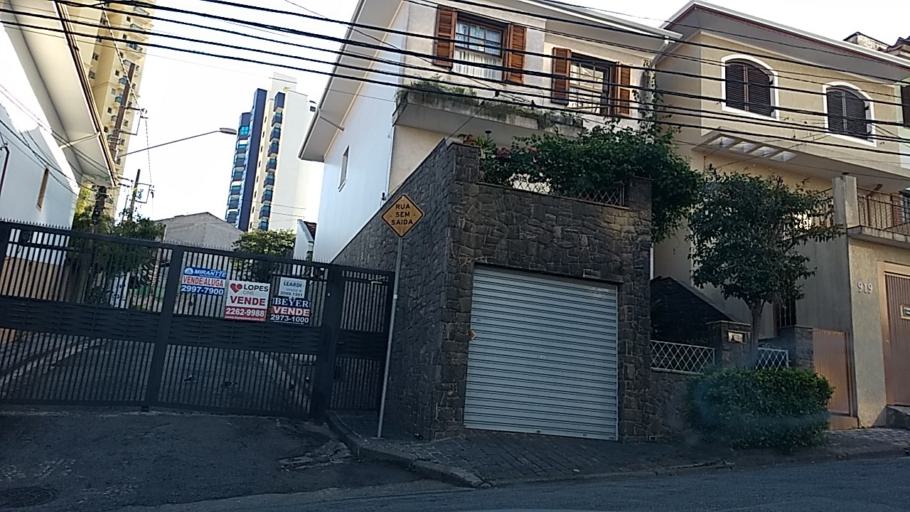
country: BR
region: Sao Paulo
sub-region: Sao Paulo
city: Sao Paulo
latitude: -23.4875
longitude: -46.6172
